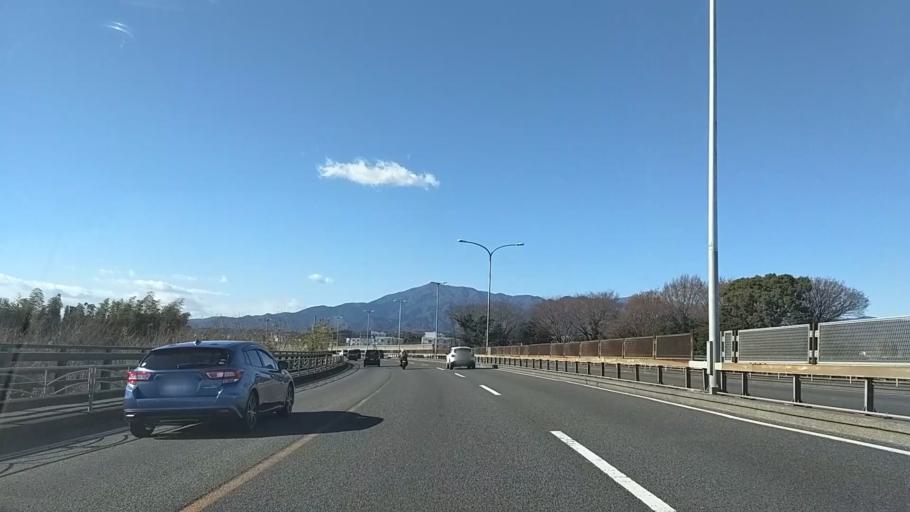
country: JP
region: Kanagawa
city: Atsugi
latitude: 35.4658
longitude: 139.3652
